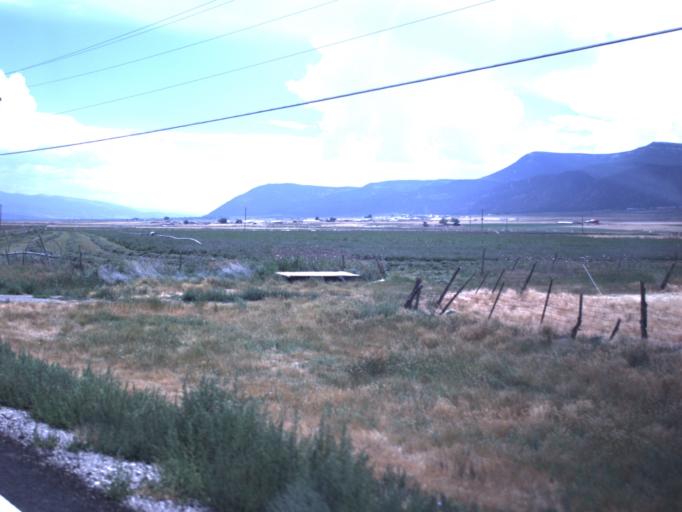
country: US
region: Utah
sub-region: Sanpete County
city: Fountain Green
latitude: 39.5907
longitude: -111.6170
